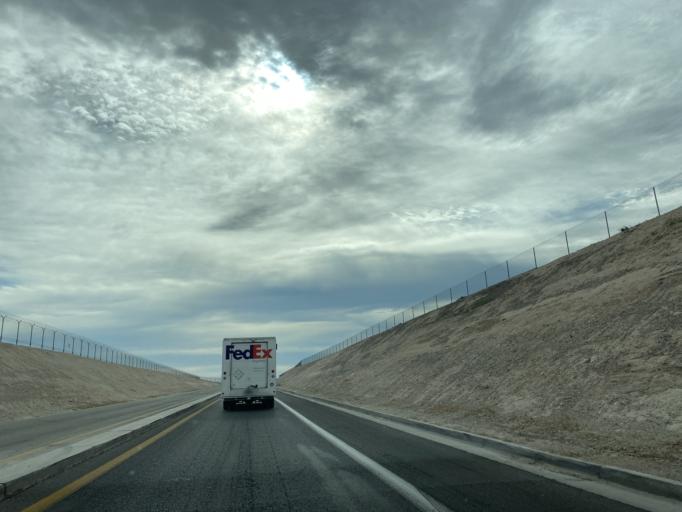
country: US
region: Nevada
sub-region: Clark County
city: Paradise
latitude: 36.0720
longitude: -115.1444
